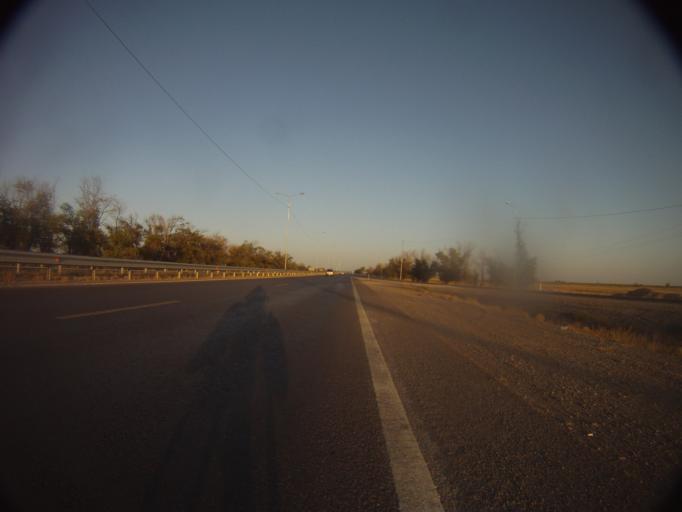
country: KZ
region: Ongtustik Qazaqstan
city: Turkestan
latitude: 43.2732
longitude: 68.3413
